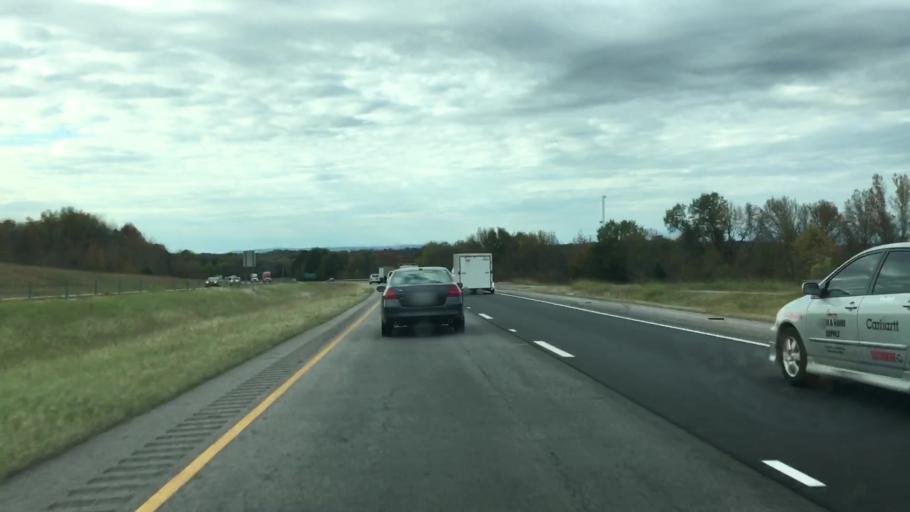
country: US
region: Arkansas
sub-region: Conway County
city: Morrilton
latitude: 35.1724
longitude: -92.6988
